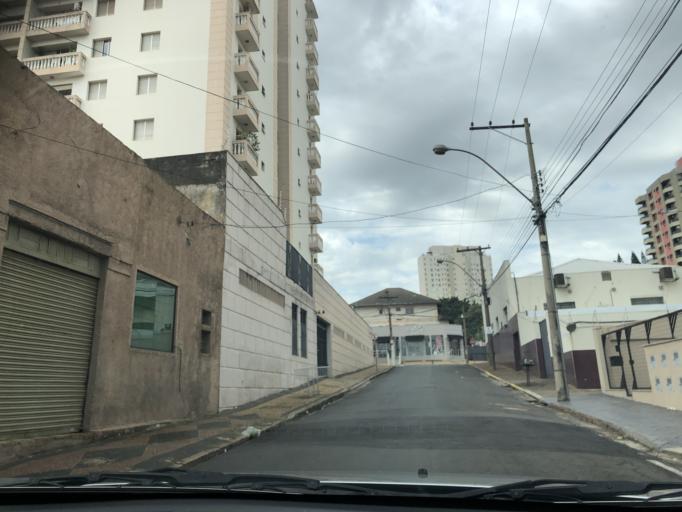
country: BR
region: Sao Paulo
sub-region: Americana
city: Americana
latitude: -22.7385
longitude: -47.3350
